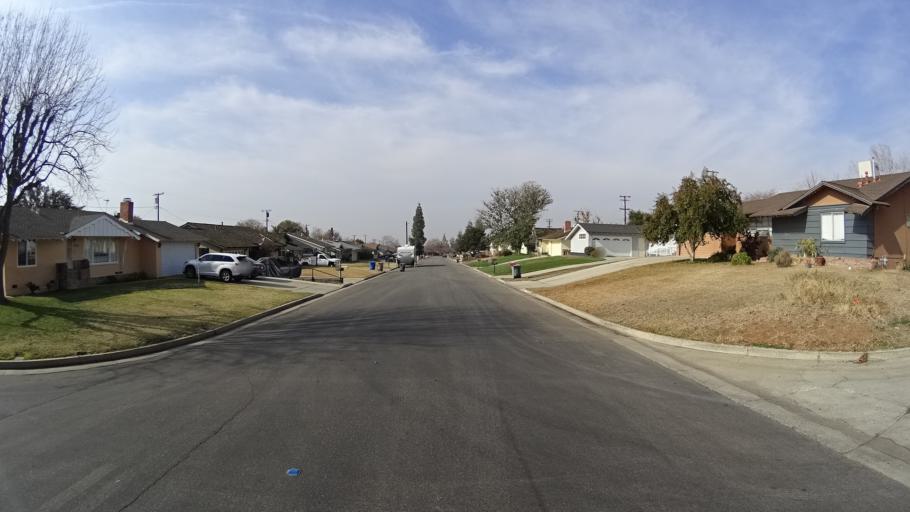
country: US
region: California
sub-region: Kern County
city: Oildale
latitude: 35.4035
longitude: -118.9631
